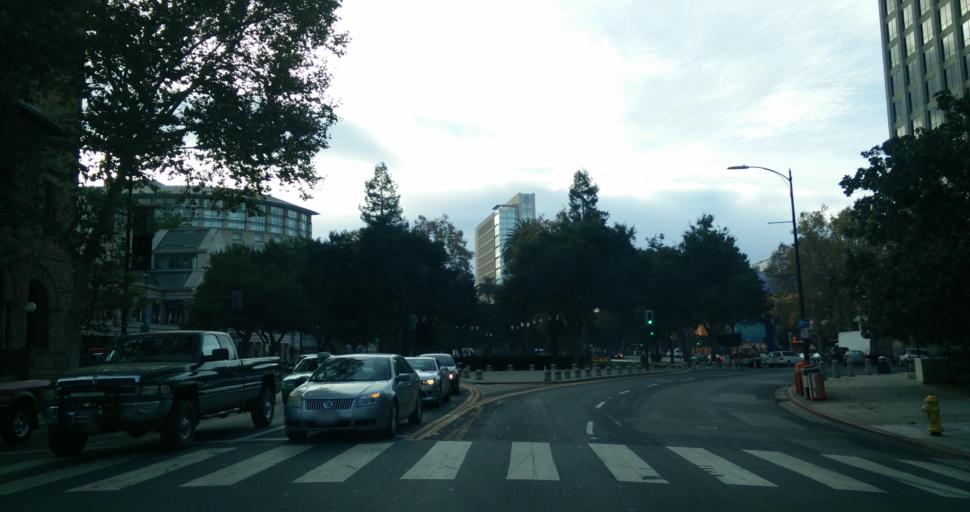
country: US
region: California
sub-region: Santa Clara County
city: San Jose
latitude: 37.3336
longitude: -121.8907
